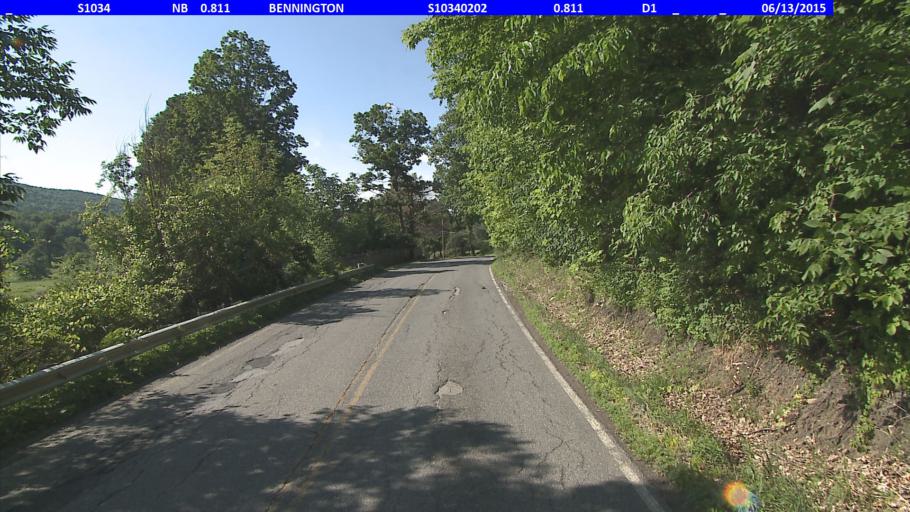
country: US
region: Vermont
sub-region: Bennington County
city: Bennington
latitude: 42.8635
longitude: -73.2070
